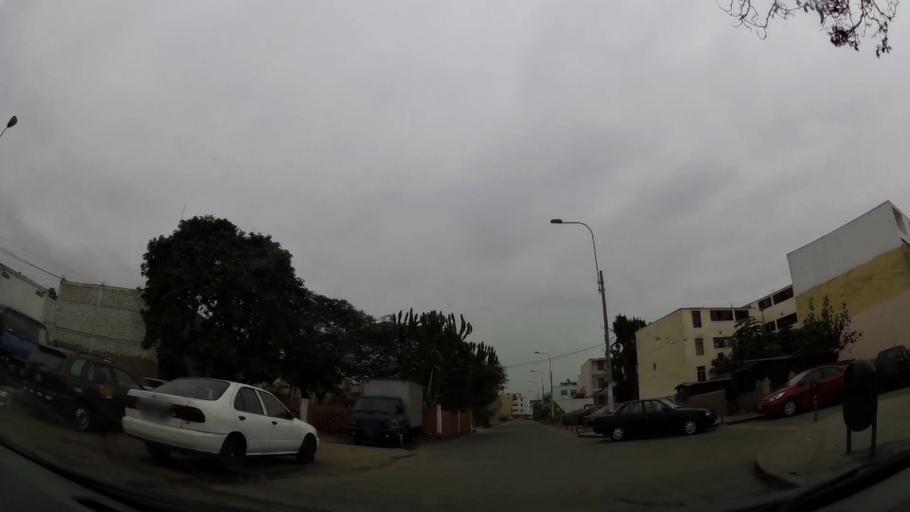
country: PE
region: Callao
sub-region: Callao
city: Callao
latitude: -12.0604
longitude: -77.0727
